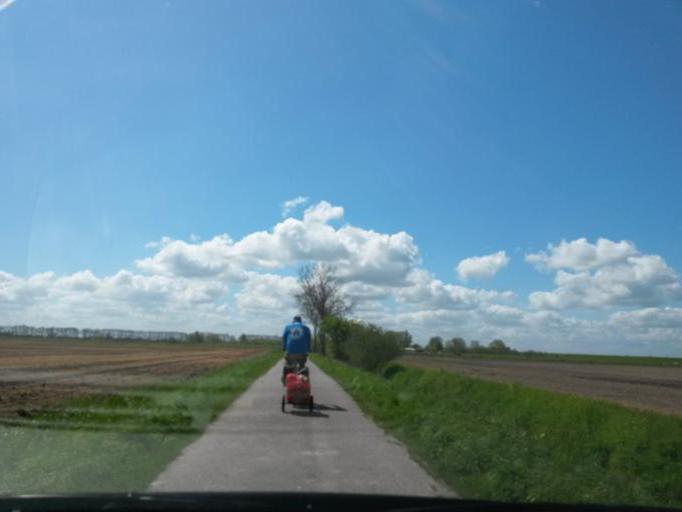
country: DE
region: Schleswig-Holstein
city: Seestermuhe
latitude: 53.6755
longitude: 9.5653
